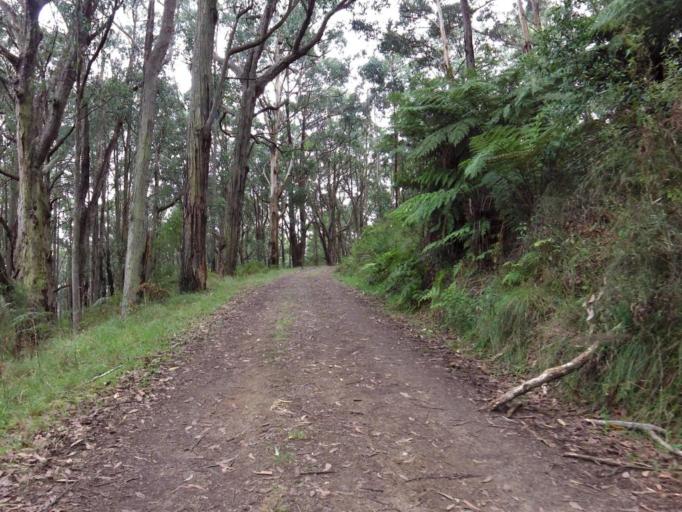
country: AU
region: Victoria
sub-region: Yarra Ranges
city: Ferny Creek
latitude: -37.8641
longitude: 145.3398
